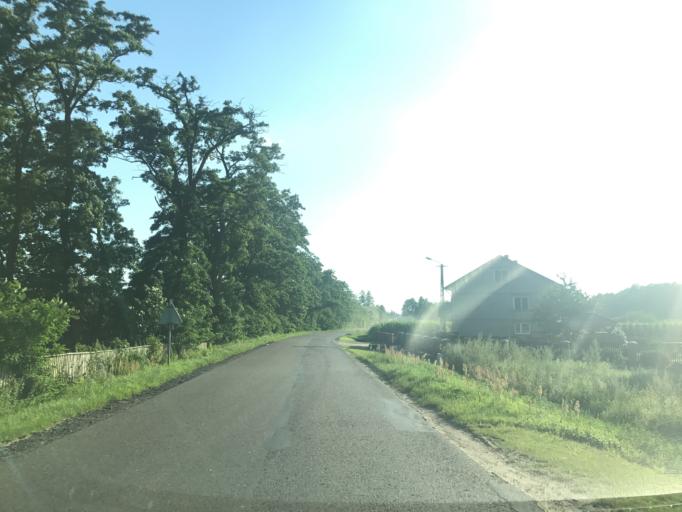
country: PL
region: Greater Poland Voivodeship
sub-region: Powiat turecki
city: Tuliszkow
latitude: 52.0854
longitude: 18.3344
